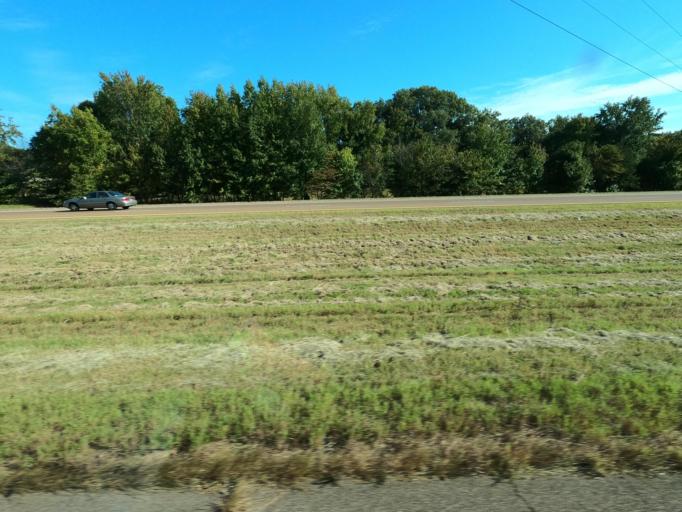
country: US
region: Tennessee
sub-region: Dyer County
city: Newbern
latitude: 36.1530
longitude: -89.2526
